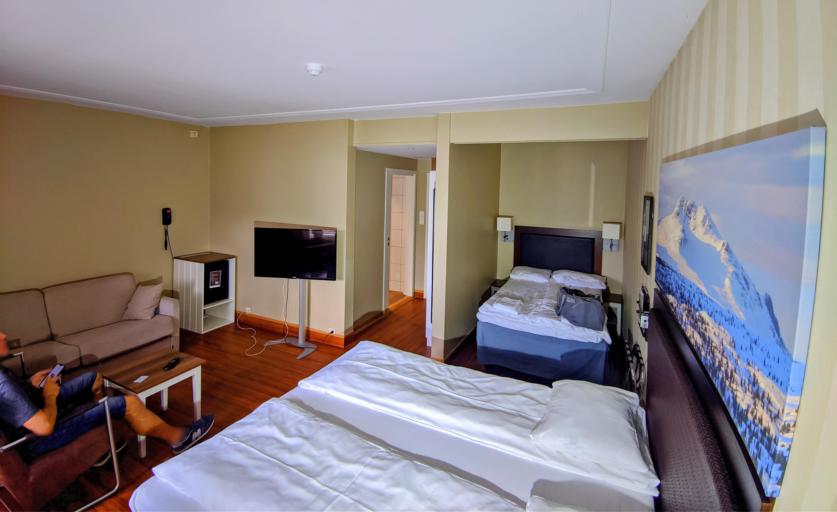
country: NO
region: Oppland
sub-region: Nord-Aurdal
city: Fagernes
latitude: 60.9849
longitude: 9.2387
